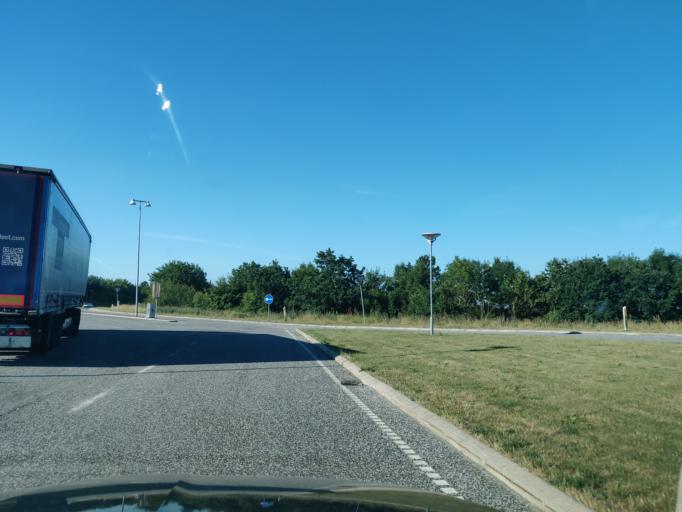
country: DK
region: Central Jutland
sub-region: Arhus Kommune
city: Sabro
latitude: 56.1778
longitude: 10.0656
